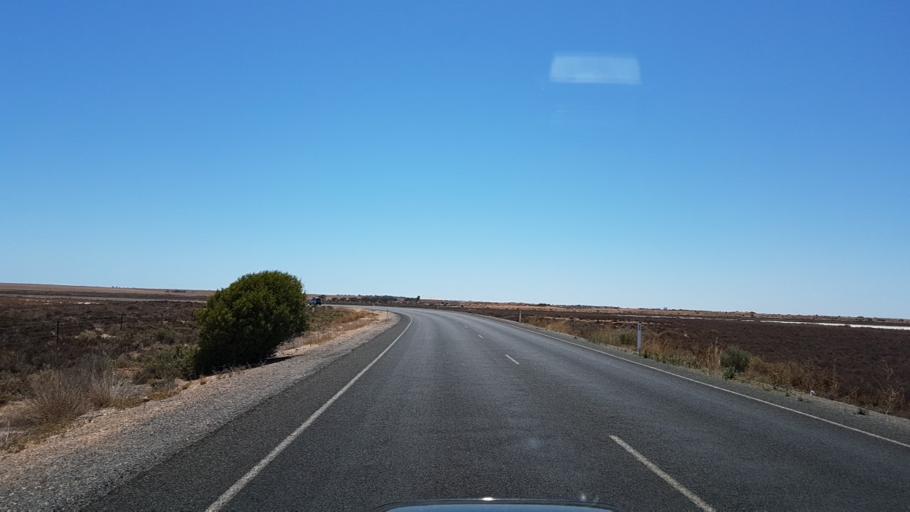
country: AU
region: South Australia
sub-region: Copper Coast
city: Wallaroo
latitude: -33.9170
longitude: 137.6464
